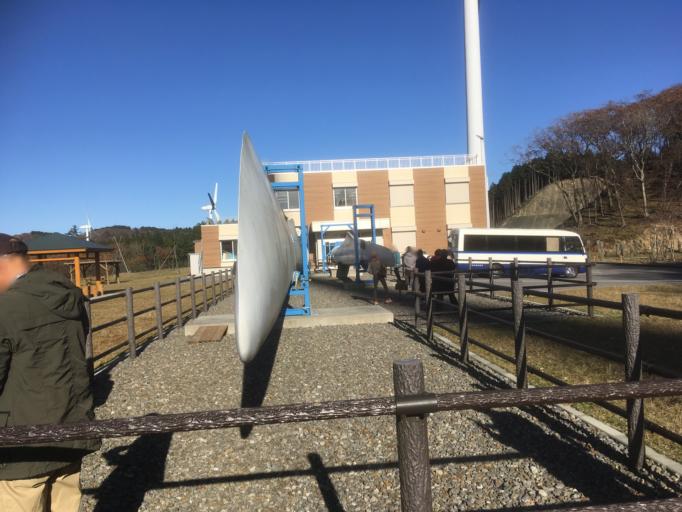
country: JP
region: Mie
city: Ueno-ebisumachi
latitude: 34.7093
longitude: 136.2796
